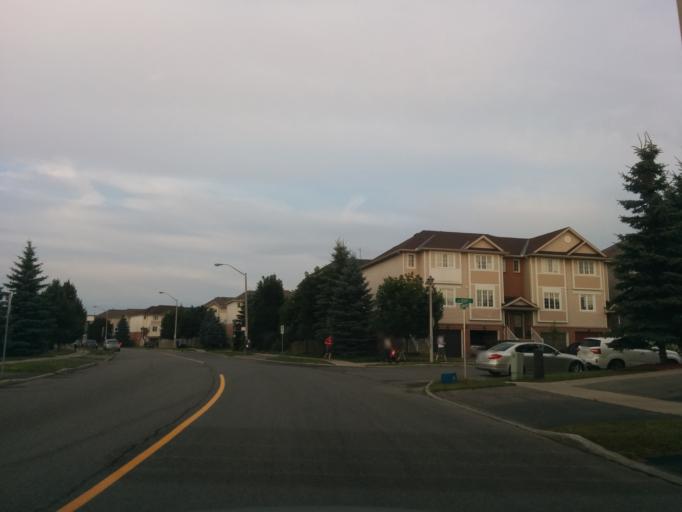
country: CA
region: Ontario
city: Ottawa
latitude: 45.3666
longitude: -75.7361
